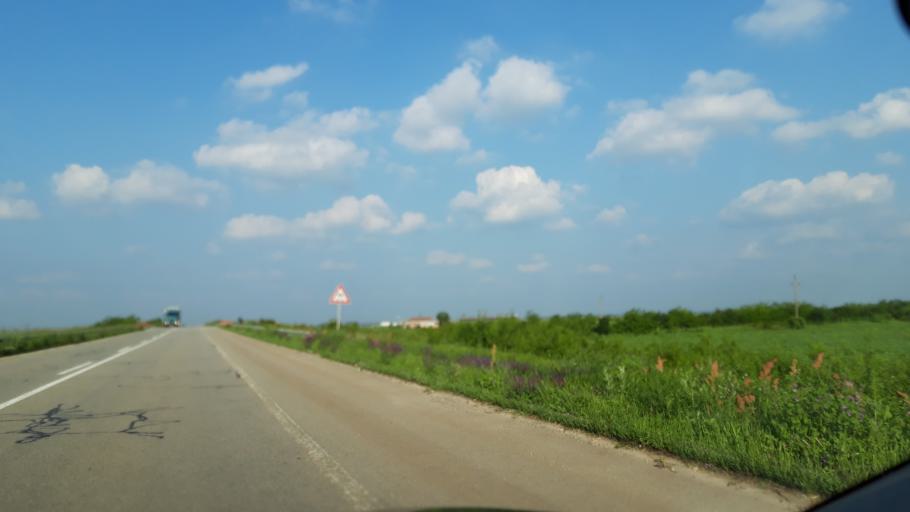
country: RS
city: Beska
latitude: 45.0929
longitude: 20.0686
